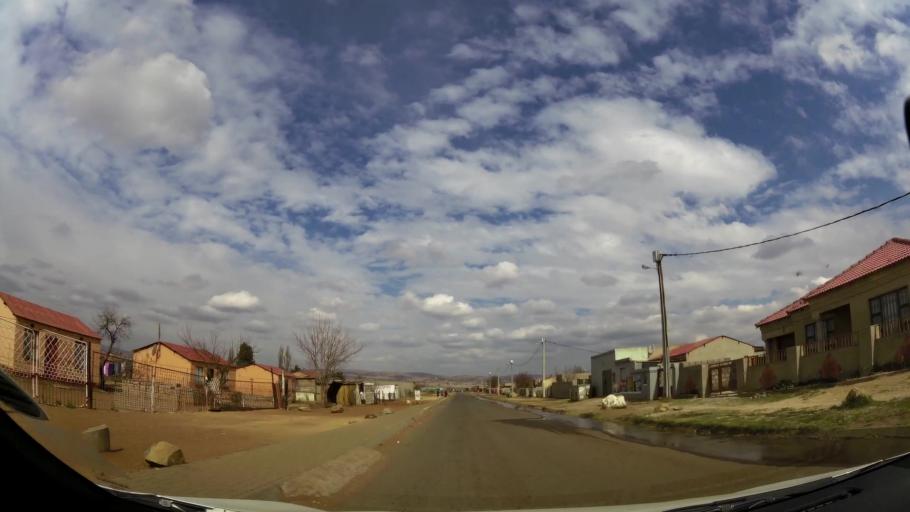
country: ZA
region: Gauteng
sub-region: Ekurhuleni Metropolitan Municipality
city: Germiston
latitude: -26.4094
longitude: 28.1646
